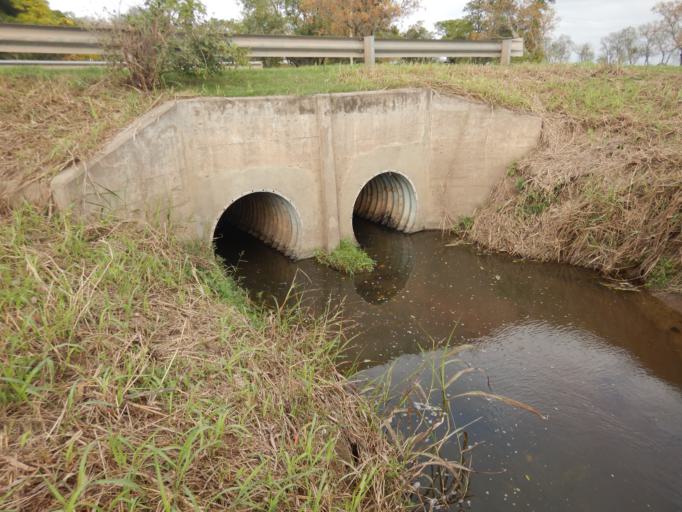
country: AR
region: Santa Fe
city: Roldan
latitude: -32.8942
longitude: -60.9714
